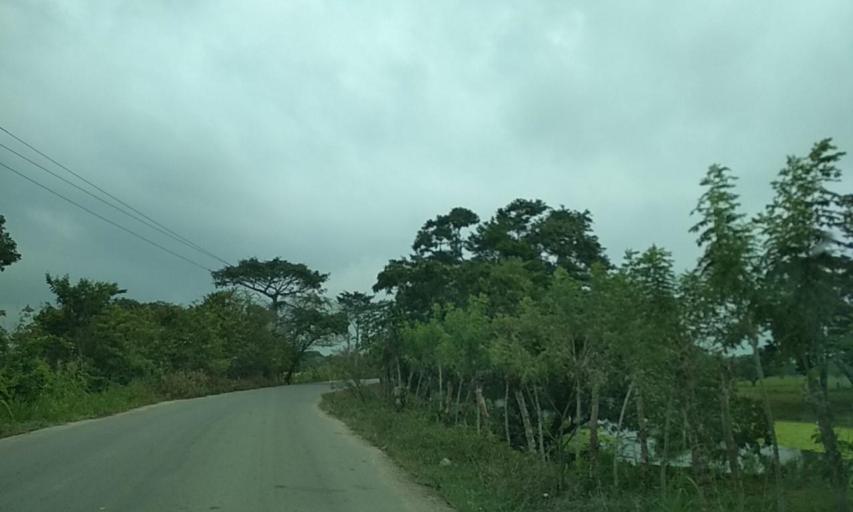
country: MX
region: Tabasco
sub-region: Huimanguillo
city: Francisco Rueda
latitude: 17.5918
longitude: -94.0913
